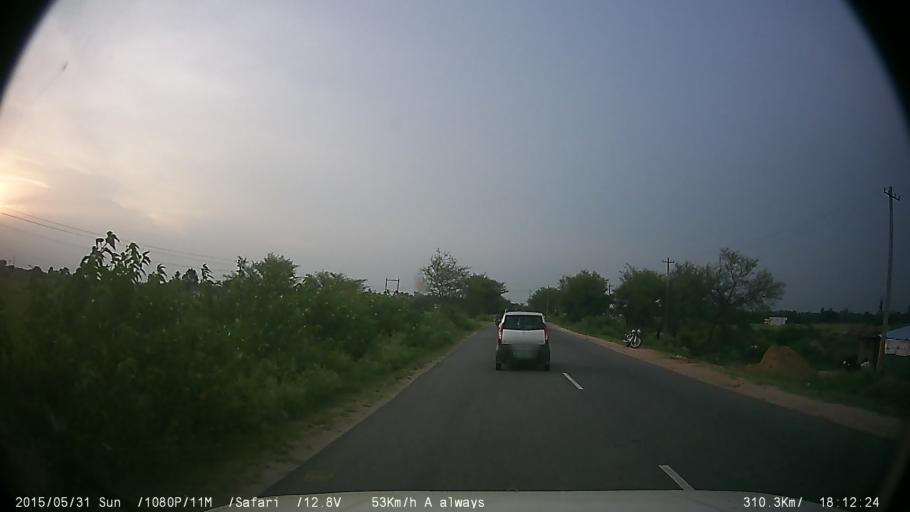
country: IN
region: Karnataka
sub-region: Mysore
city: Nanjangud
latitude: 12.0956
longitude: 76.6722
